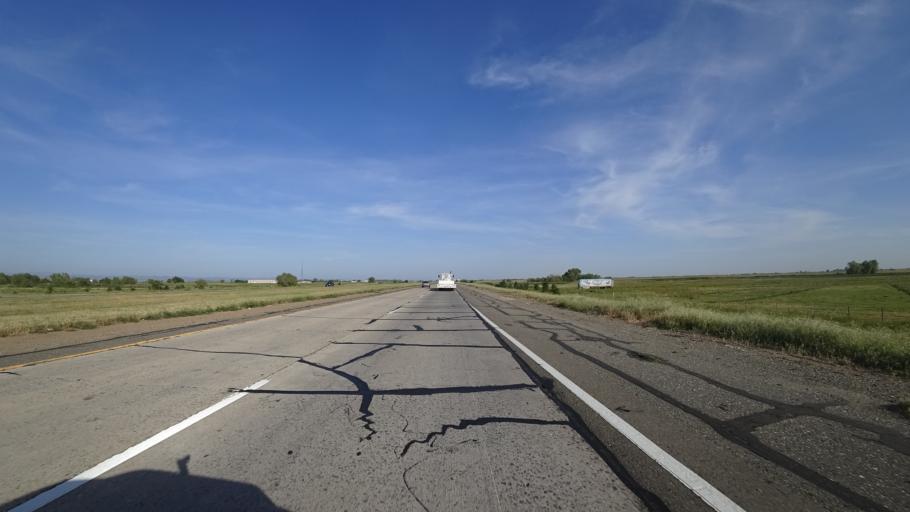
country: US
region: California
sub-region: Yuba County
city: Olivehurst
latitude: 39.0609
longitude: -121.5085
